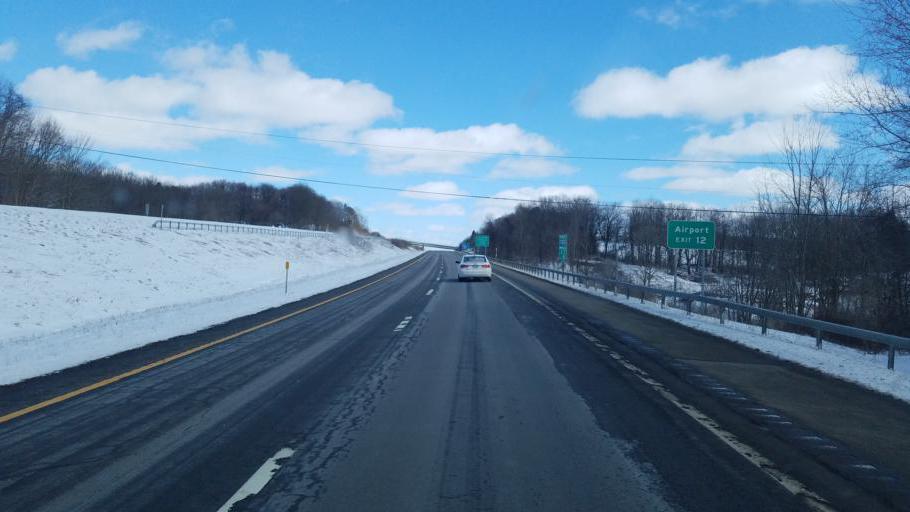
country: US
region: New York
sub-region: Chautauqua County
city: Jamestown
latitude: 42.1200
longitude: -79.2547
